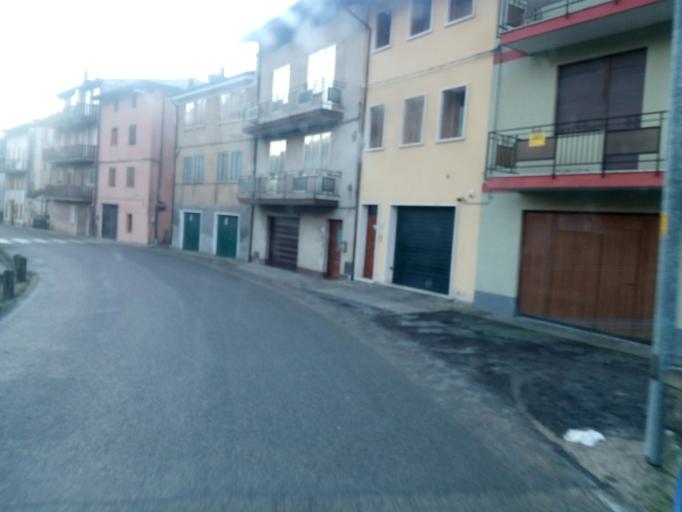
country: IT
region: Veneto
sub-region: Provincia di Vicenza
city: Valli del Pasubio
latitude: 45.7449
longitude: 11.2385
